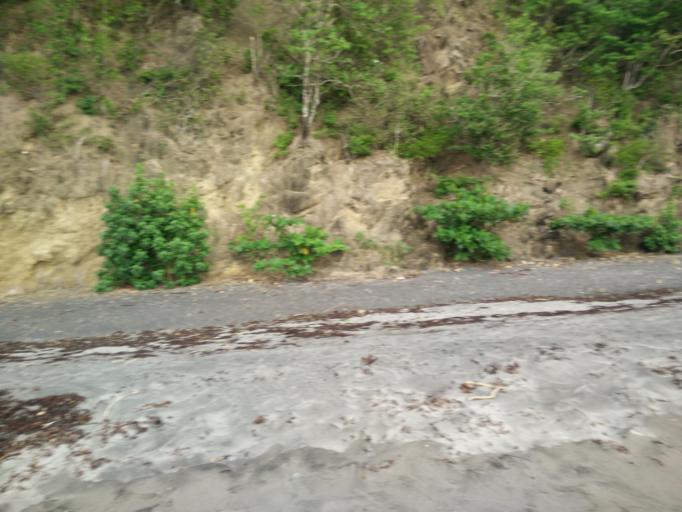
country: MQ
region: Martinique
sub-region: Martinique
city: Basse-Pointe
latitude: 14.8428
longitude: -61.2189
